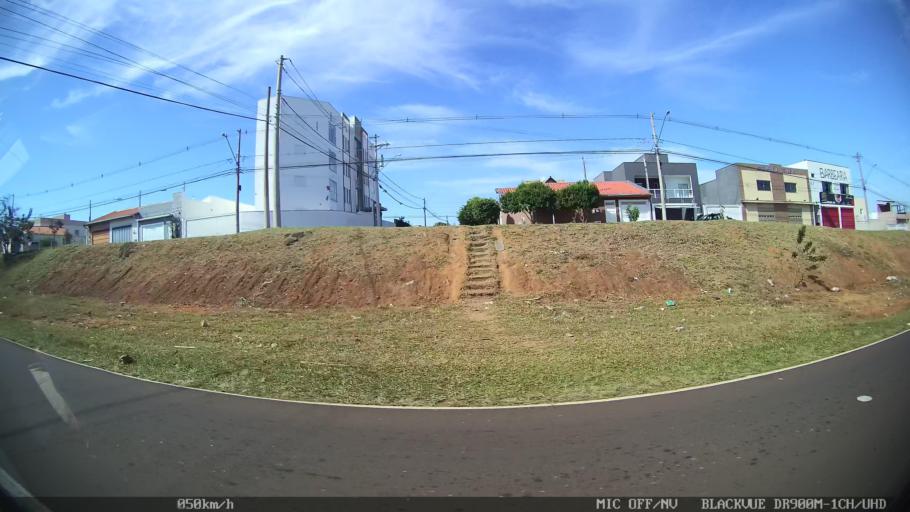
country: BR
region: Sao Paulo
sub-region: Franca
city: Franca
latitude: -20.5133
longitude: -47.4401
